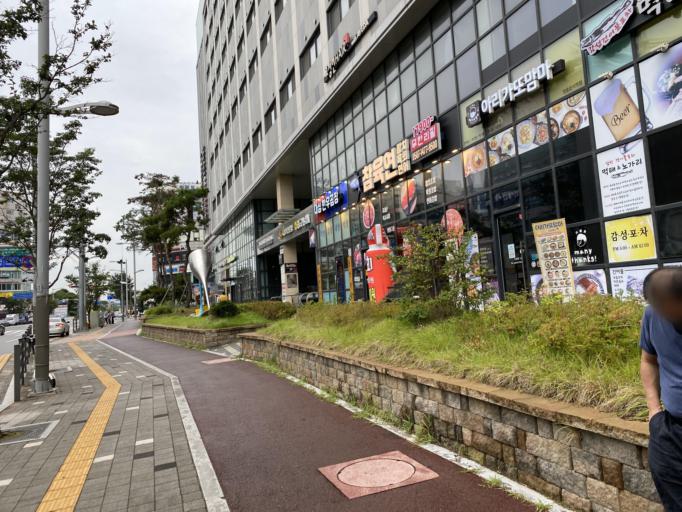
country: KR
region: Incheon
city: Incheon
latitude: 37.4930
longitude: 126.4903
